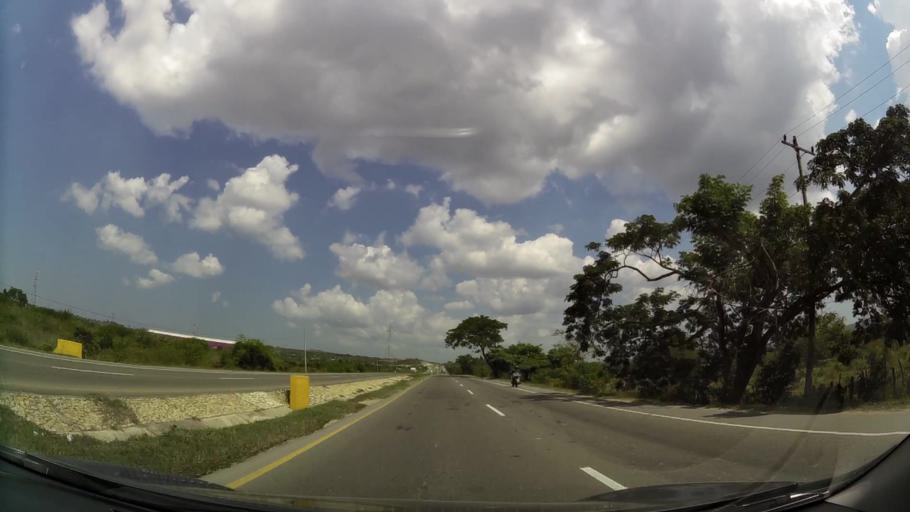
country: CO
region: Bolivar
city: Cartagena
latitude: 10.3545
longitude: -75.4762
